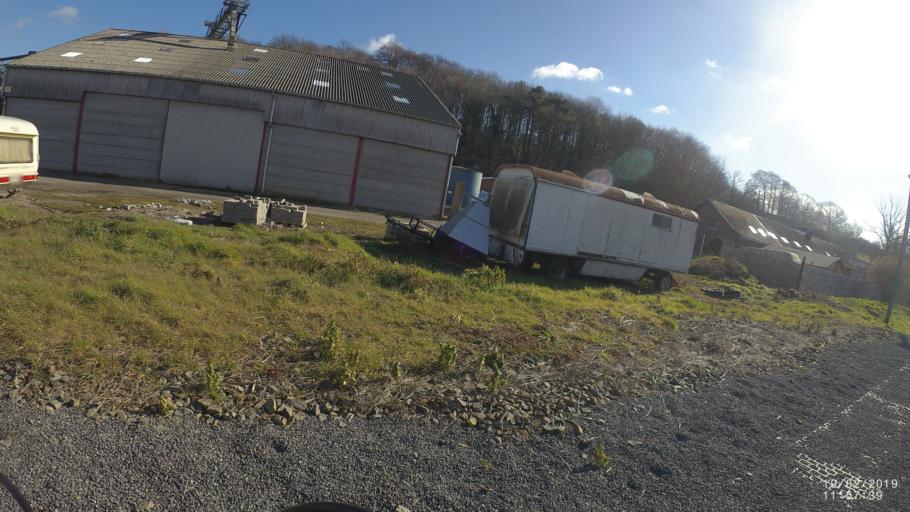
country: BE
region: Wallonia
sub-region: Province de Liege
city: Juprelle
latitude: 50.7493
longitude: 5.5354
